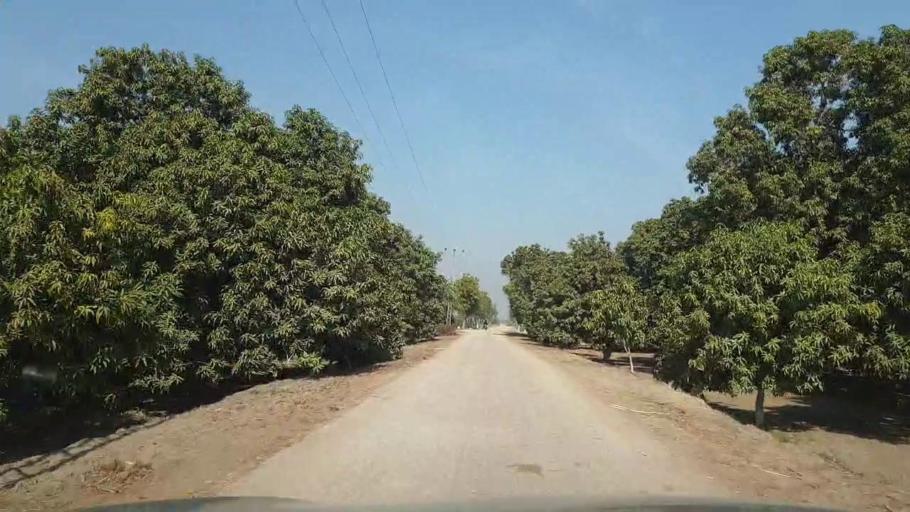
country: PK
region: Sindh
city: Tando Adam
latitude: 25.6275
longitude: 68.7383
